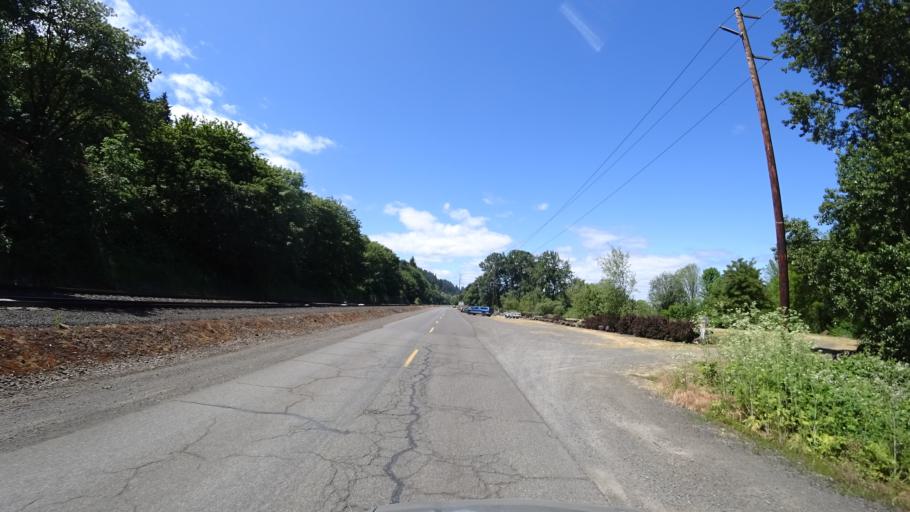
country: US
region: Oregon
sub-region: Washington County
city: Oak Hills
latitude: 45.6167
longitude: -122.8039
